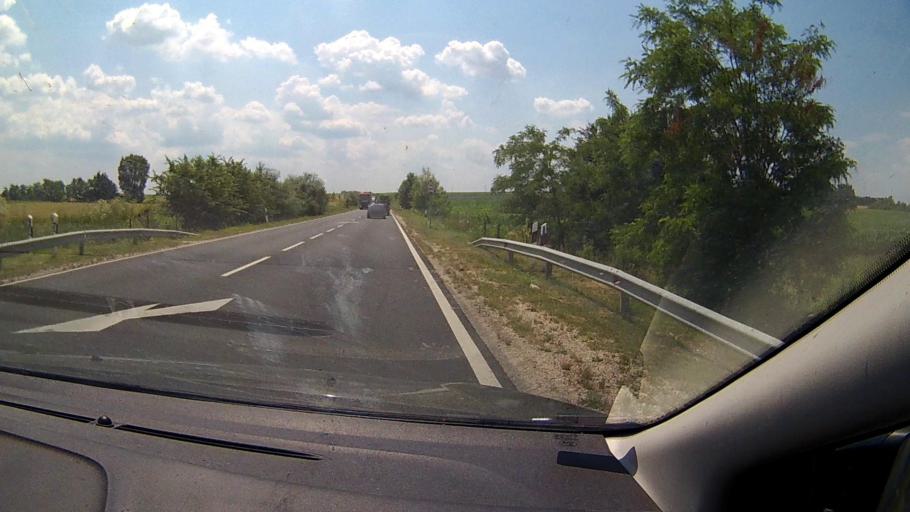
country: HU
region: Komarom-Esztergom
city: Tata
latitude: 47.6046
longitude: 18.3180
